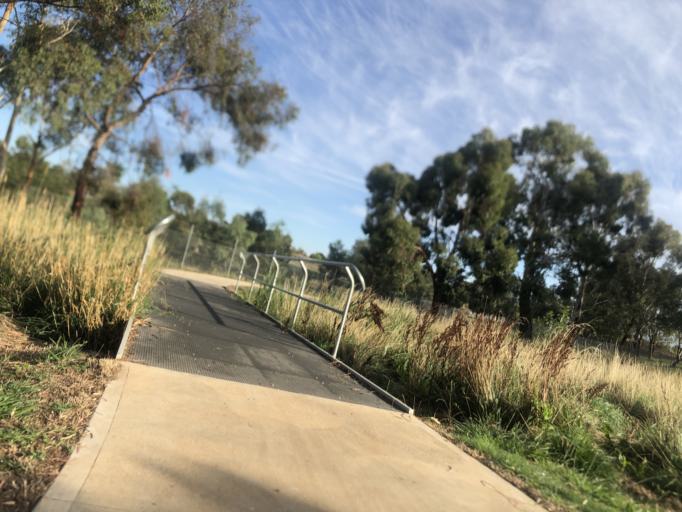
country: AU
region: New South Wales
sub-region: Orange Municipality
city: Orange
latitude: -33.3010
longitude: 149.0922
